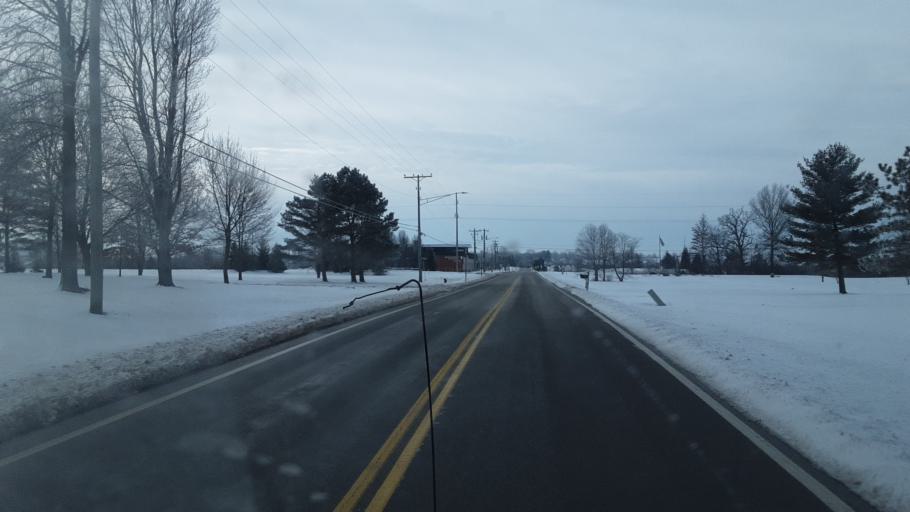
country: US
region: Ohio
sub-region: Union County
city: Marysville
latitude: 40.2159
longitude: -83.3745
